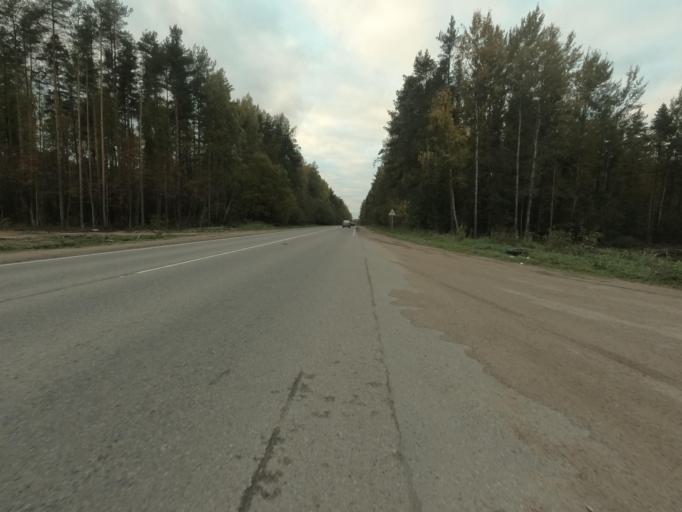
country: RU
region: Leningrad
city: Pavlovo
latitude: 59.8058
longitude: 30.9340
